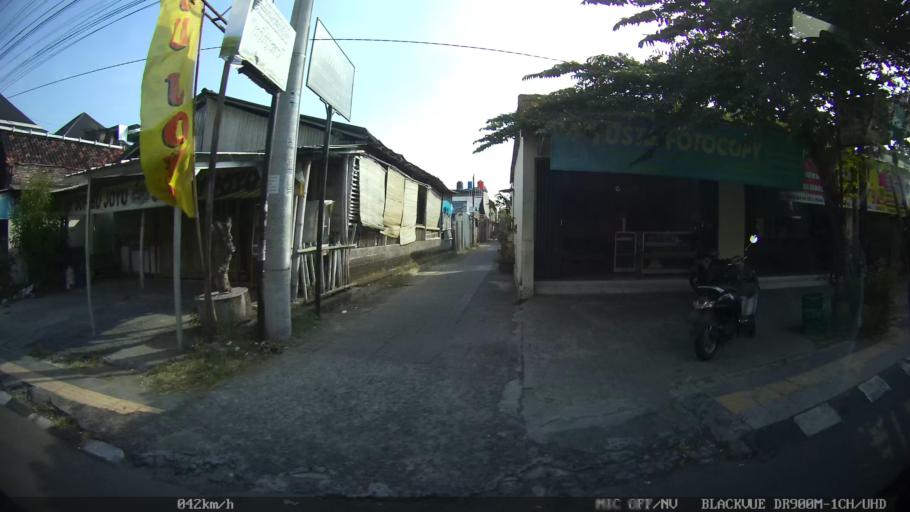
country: ID
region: Daerah Istimewa Yogyakarta
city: Yogyakarta
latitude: -7.8202
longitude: 110.3883
